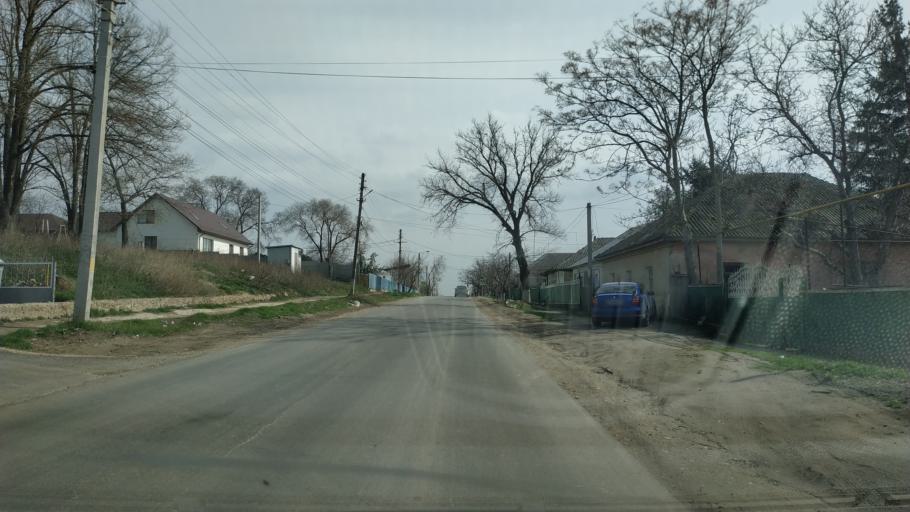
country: MD
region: Gagauzia
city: Vulcanesti
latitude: 45.6751
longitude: 28.4172
